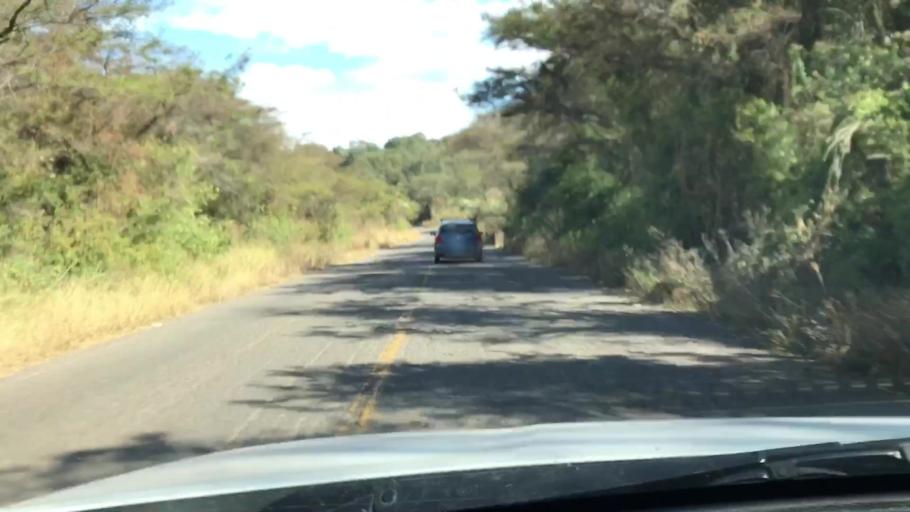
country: MX
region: Jalisco
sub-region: Zacoalco de Torres
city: Barranca de Otates (Barranca de Otatan)
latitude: 20.1952
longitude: -103.7151
